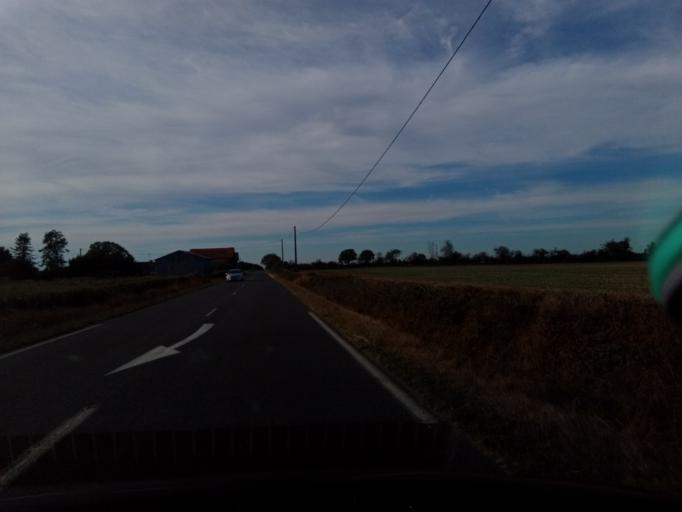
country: FR
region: Poitou-Charentes
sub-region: Departement de la Vienne
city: Saulge
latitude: 46.4073
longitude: 0.8898
